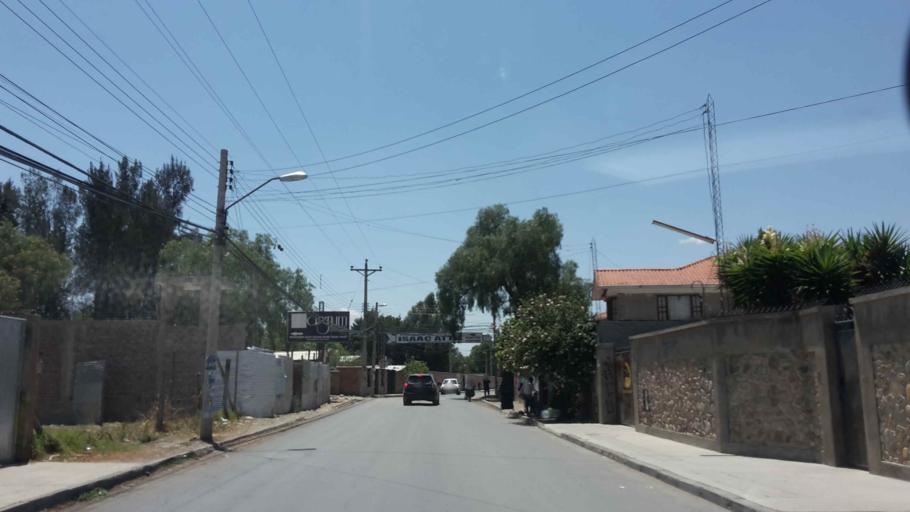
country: BO
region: Cochabamba
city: Cochabamba
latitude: -17.3676
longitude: -66.1956
